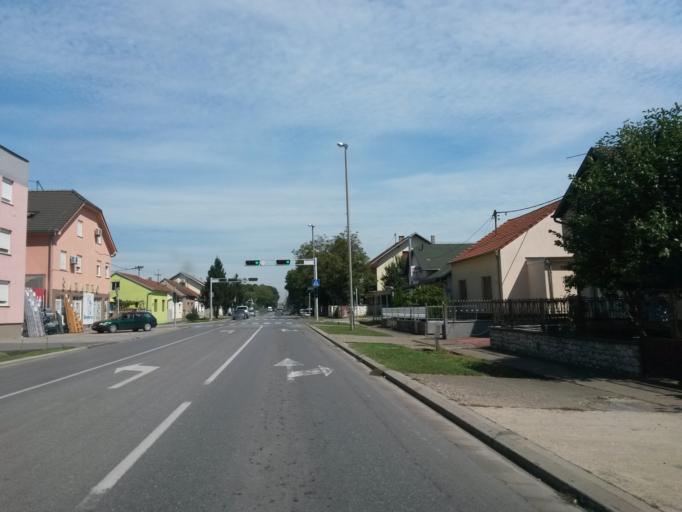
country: HR
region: Vukovarsko-Srijemska
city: Vinkovci
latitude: 45.2765
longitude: 18.7974
